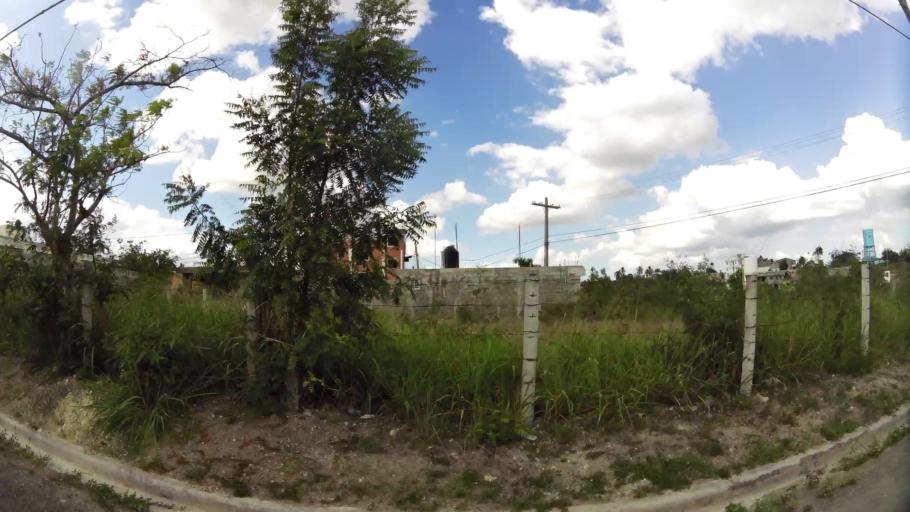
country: DO
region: Nacional
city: Ensanche Luperon
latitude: 18.5292
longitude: -69.8950
